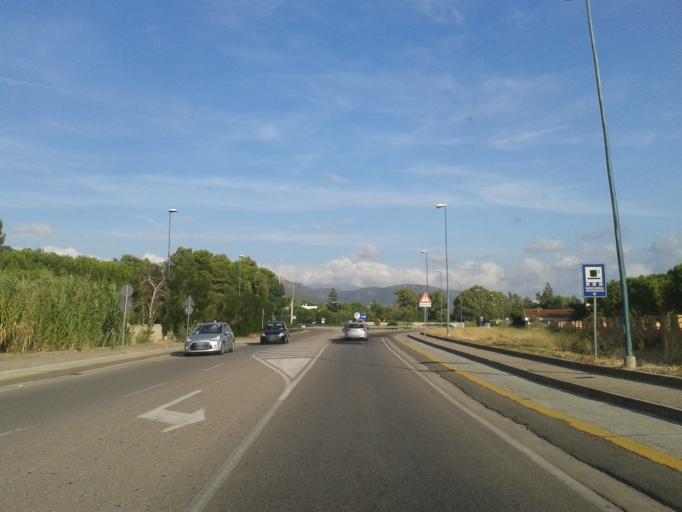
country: IT
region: Sardinia
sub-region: Provincia di Cagliari
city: Quartu Sant'Elena
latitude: 39.2188
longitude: 9.2835
